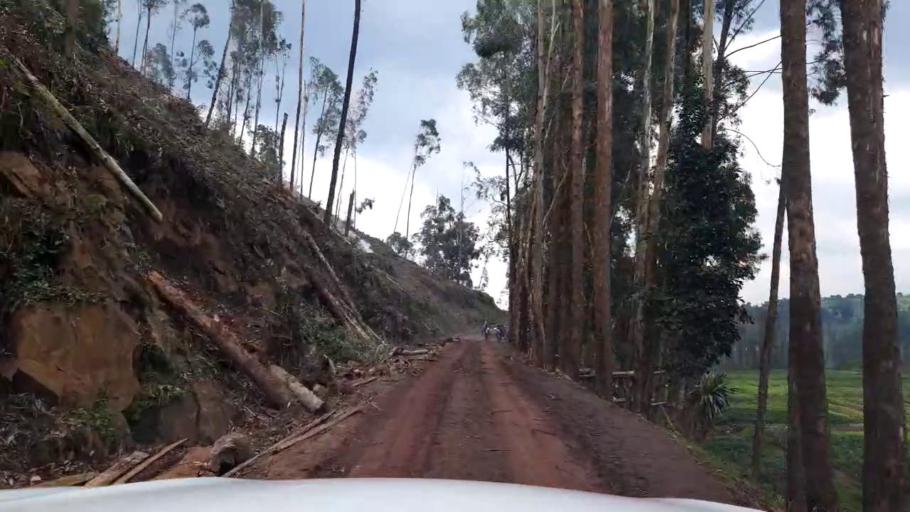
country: UG
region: Western Region
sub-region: Kisoro District
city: Kisoro
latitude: -1.3847
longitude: 29.7993
